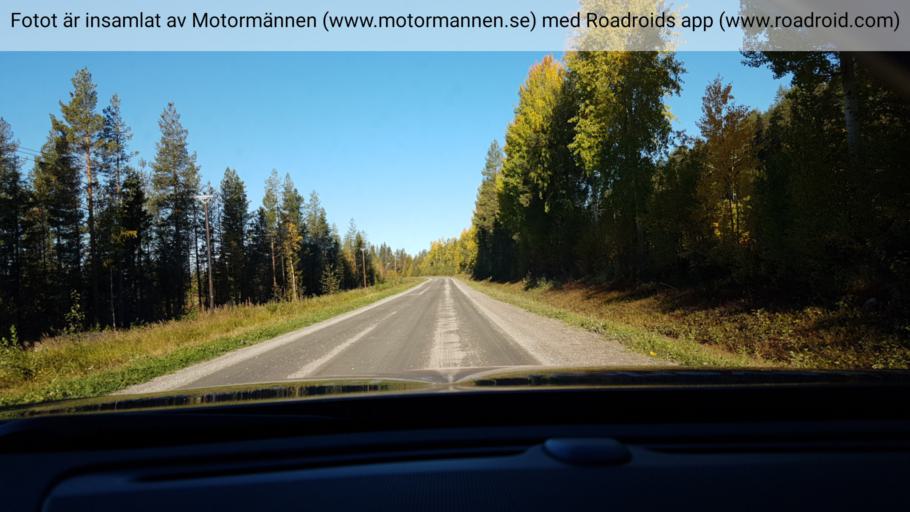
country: SE
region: Norrbotten
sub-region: Alvsbyns Kommun
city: AElvsbyn
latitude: 66.1779
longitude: 21.2361
